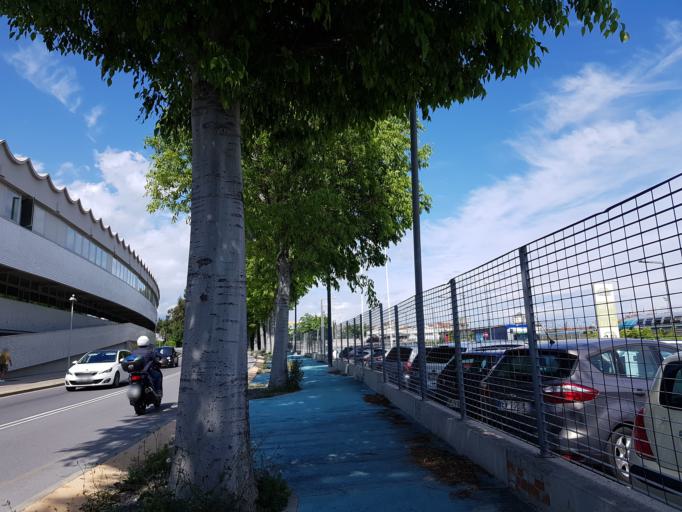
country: IT
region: Liguria
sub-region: Provincia di Savona
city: Savona
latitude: 44.2991
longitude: 8.4634
